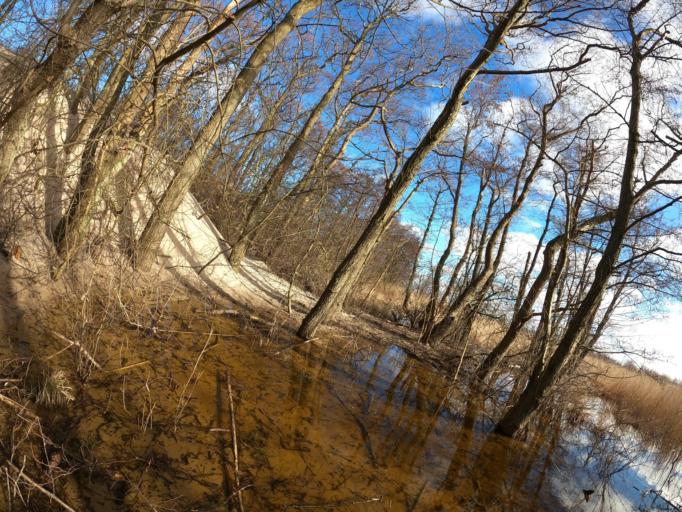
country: PL
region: West Pomeranian Voivodeship
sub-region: Powiat koszalinski
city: Sianow
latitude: 54.3243
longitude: 16.2215
